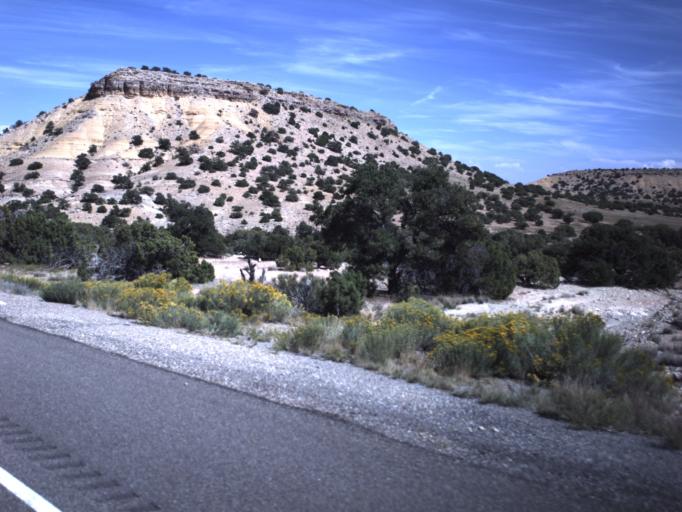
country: US
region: Utah
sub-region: Emery County
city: Castle Dale
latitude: 38.9117
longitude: -110.5236
